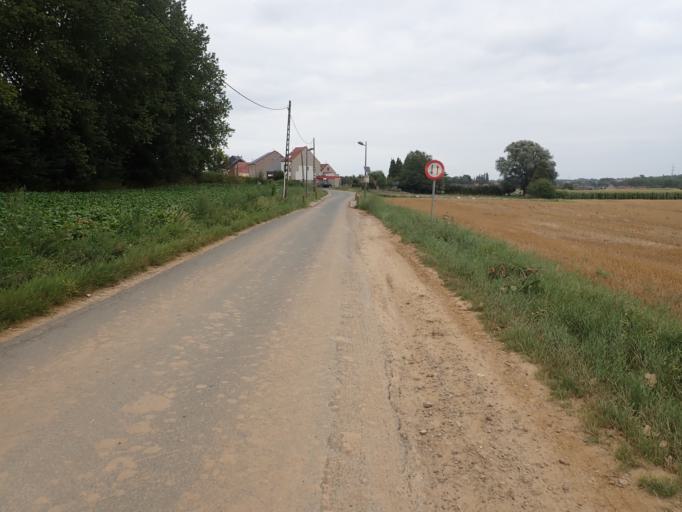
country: BE
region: Flanders
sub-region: Provincie Vlaams-Brabant
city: Asse
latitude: 50.9283
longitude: 4.2042
